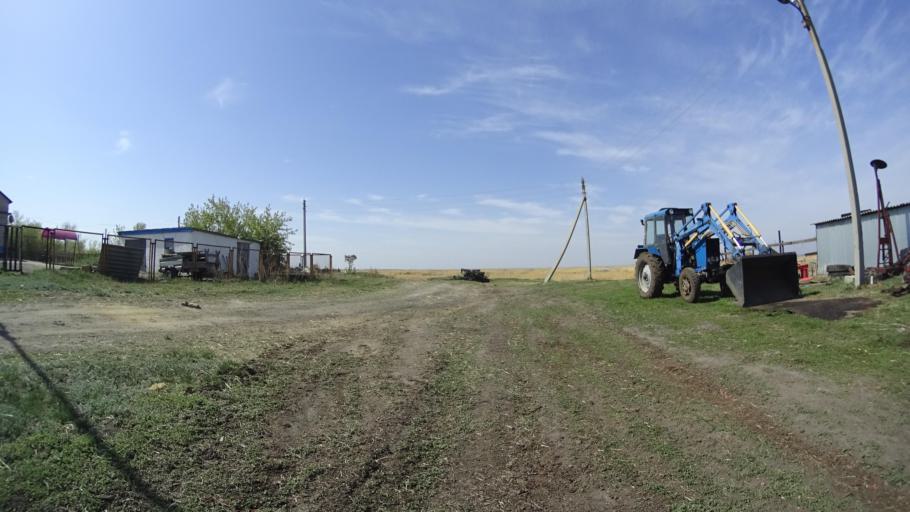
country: RU
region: Chelyabinsk
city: Chesma
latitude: 53.7915
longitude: 61.0359
